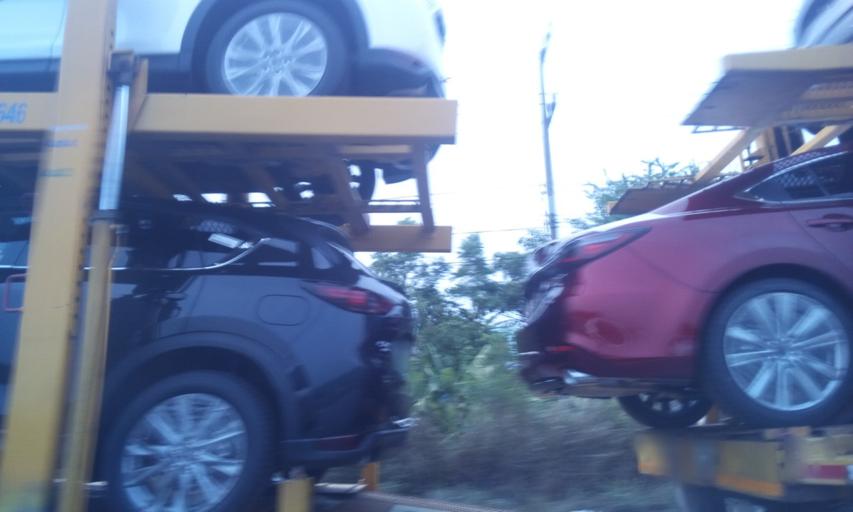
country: TH
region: Chon Buri
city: Ban Bueng
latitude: 13.2424
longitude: 101.2428
